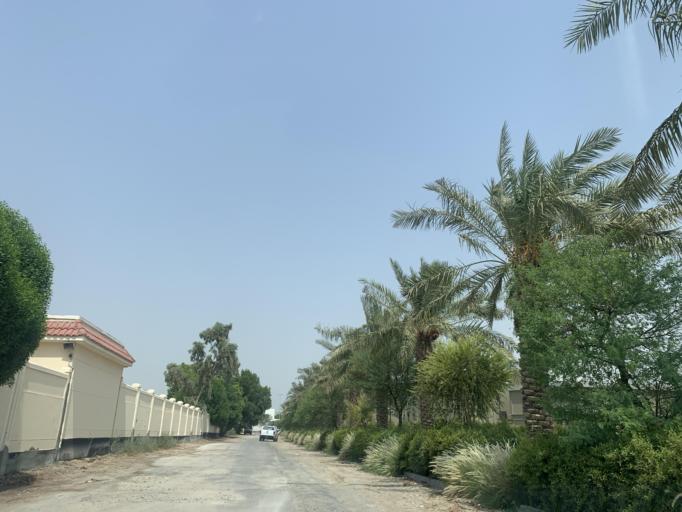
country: BH
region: Central Governorate
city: Madinat Hamad
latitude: 26.1644
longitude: 50.4684
